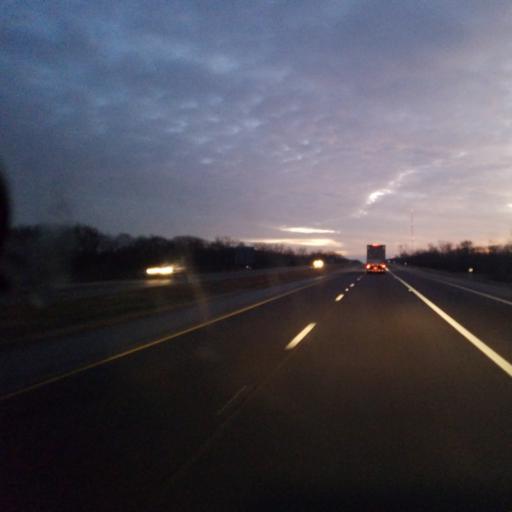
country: US
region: Illinois
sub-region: Tazewell County
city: Marquette Heights
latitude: 40.6300
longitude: -89.5898
